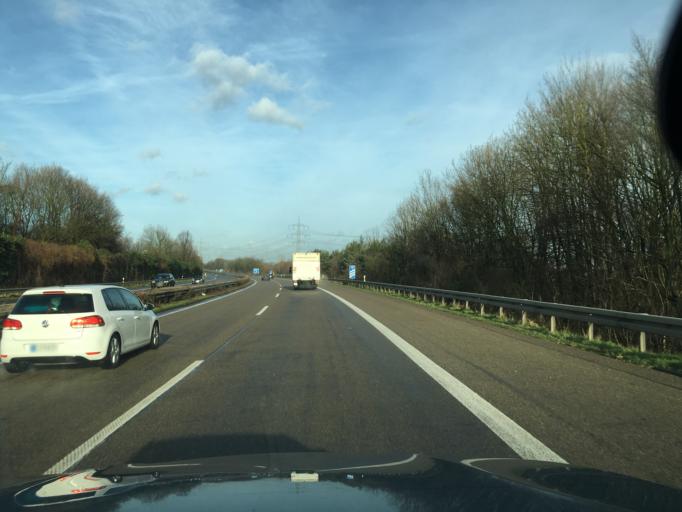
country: DE
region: North Rhine-Westphalia
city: Bruhl
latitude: 50.8230
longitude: 6.9340
